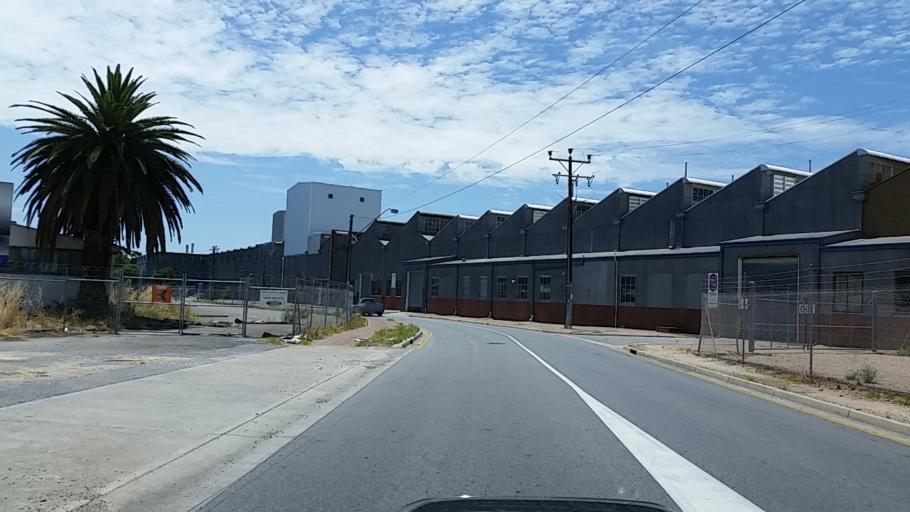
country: AU
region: South Australia
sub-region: Charles Sturt
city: Woodville North
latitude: -34.8653
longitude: 138.5382
